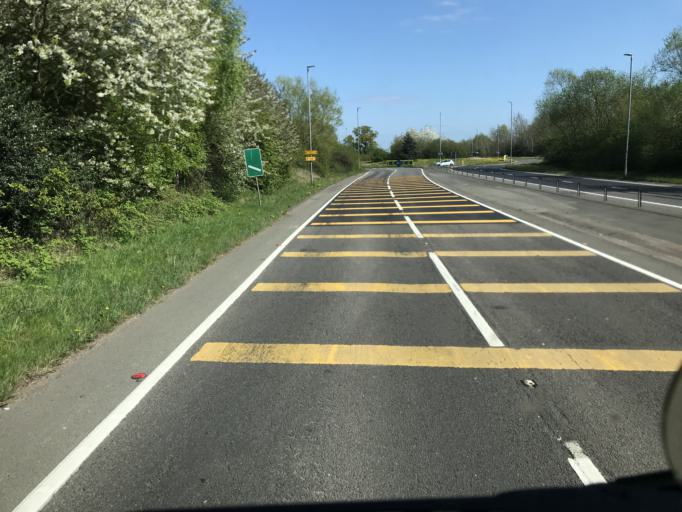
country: GB
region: England
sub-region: Cheshire East
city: Crewe
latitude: 53.0712
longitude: -2.4406
